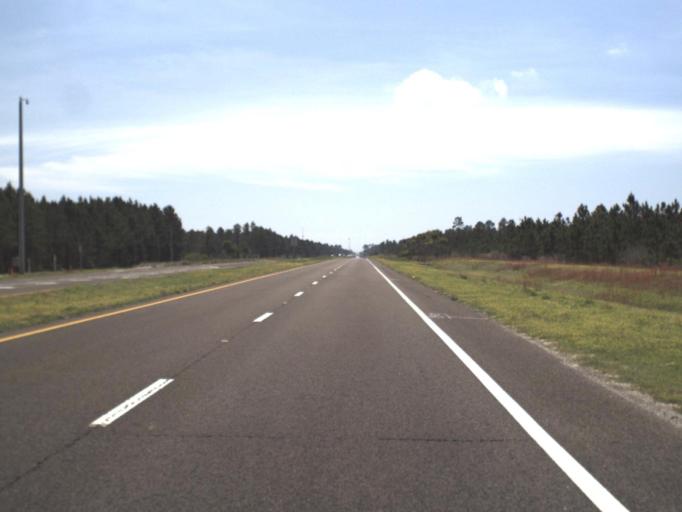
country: US
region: Florida
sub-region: Bay County
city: Laguna Beach
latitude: 30.2556
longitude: -85.8769
